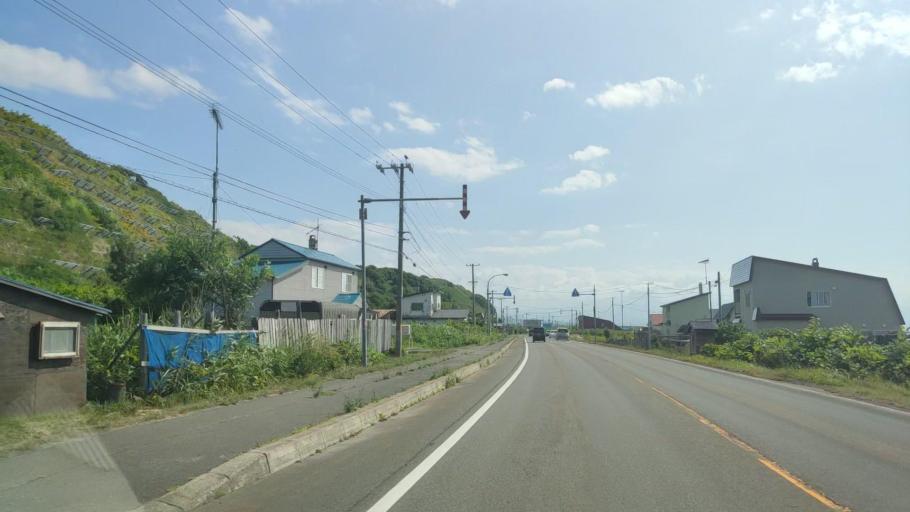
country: JP
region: Hokkaido
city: Rumoi
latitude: 43.9849
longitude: 141.6483
